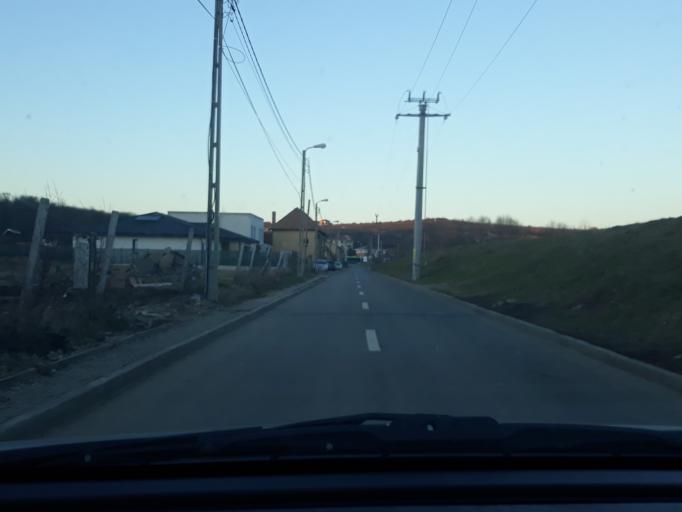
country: RO
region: Bihor
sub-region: Comuna Biharea
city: Oradea
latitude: 47.0807
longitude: 21.9454
